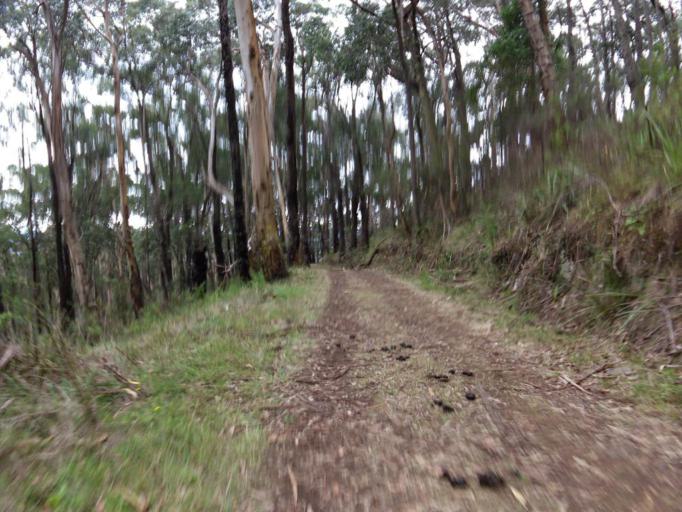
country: AU
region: Victoria
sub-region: Yarra Ranges
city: Ferny Creek
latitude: -37.8659
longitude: 145.3331
